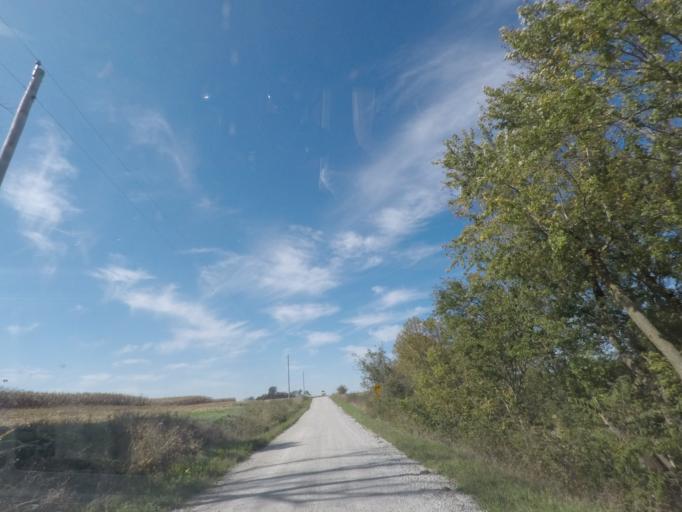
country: US
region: Iowa
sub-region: Story County
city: Nevada
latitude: 42.0125
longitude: -93.3554
